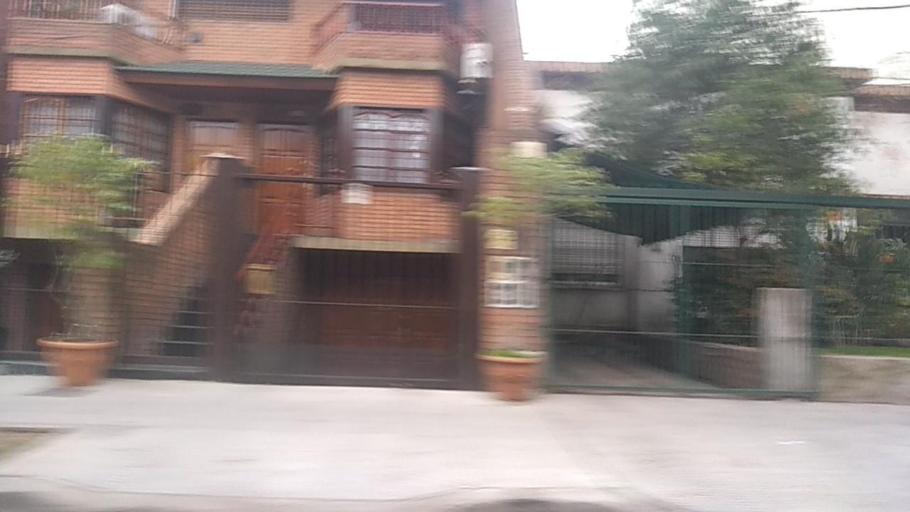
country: AR
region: Buenos Aires F.D.
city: Villa Santa Rita
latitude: -34.5993
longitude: -58.4962
